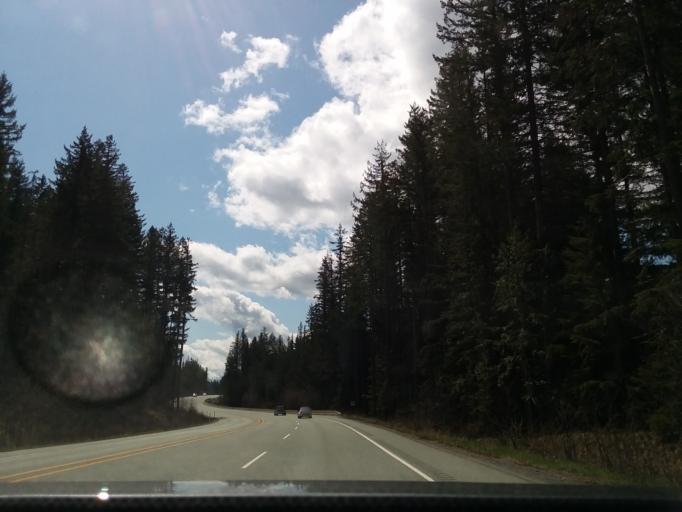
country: CA
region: British Columbia
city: Whistler
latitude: 49.9986
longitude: -123.1344
